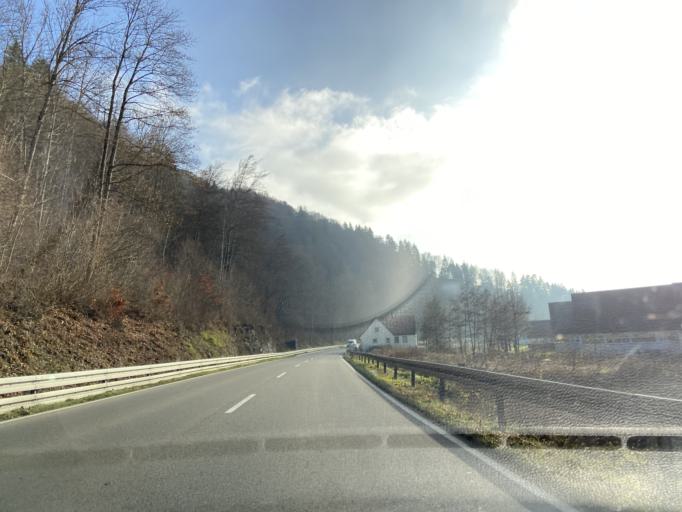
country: DE
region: Baden-Wuerttemberg
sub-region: Tuebingen Region
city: Hettingen
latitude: 48.2250
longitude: 9.2367
